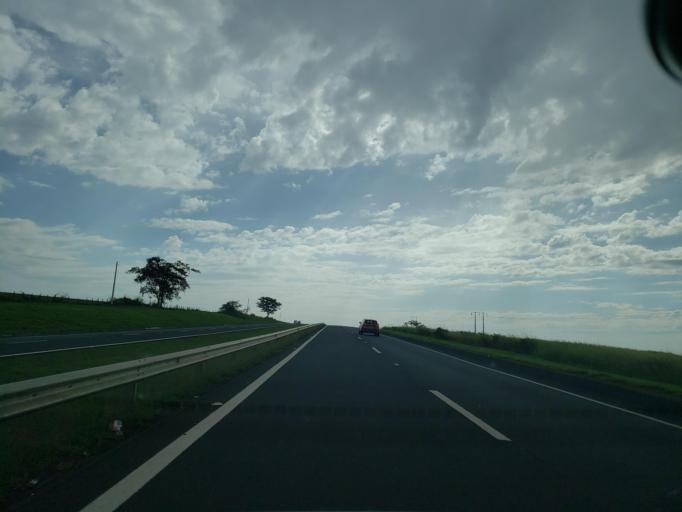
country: BR
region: Sao Paulo
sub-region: Cafelandia
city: Cafelandia
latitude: -21.7524
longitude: -49.6837
